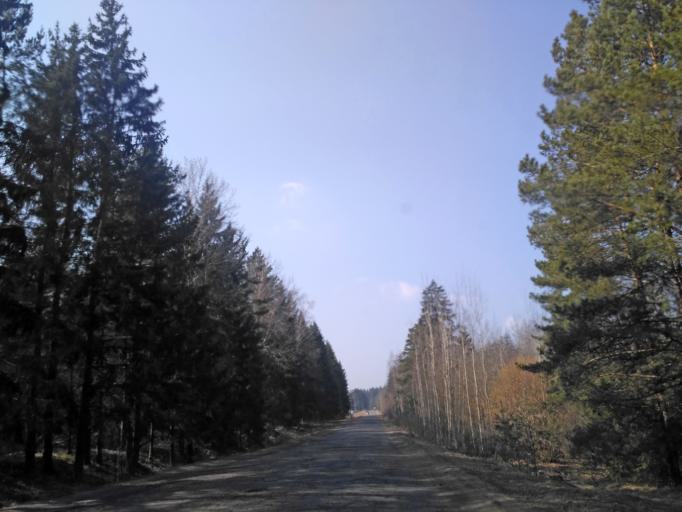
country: BY
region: Minsk
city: Horad Barysaw
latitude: 54.2475
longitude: 28.4616
